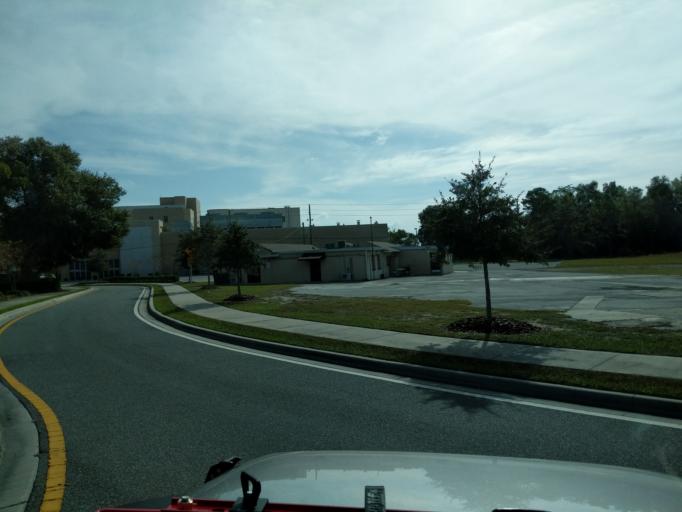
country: US
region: Florida
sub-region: Lake County
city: Tavares
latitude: 28.8051
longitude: -81.7331
